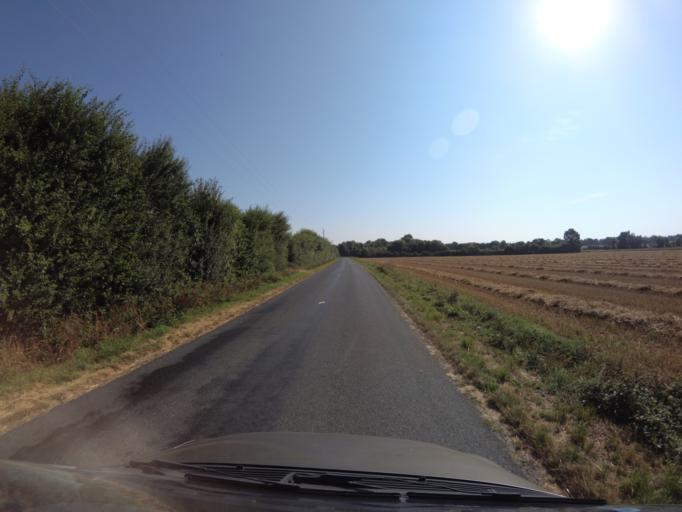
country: FR
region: Pays de la Loire
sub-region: Departement de la Vendee
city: Montaigu
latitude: 47.0034
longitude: -1.3023
